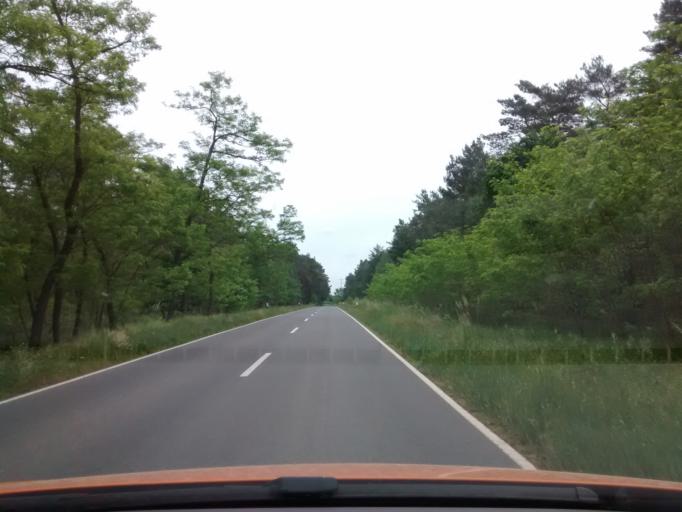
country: DE
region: Saxony-Anhalt
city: Holzdorf
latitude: 51.8354
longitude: 13.1805
